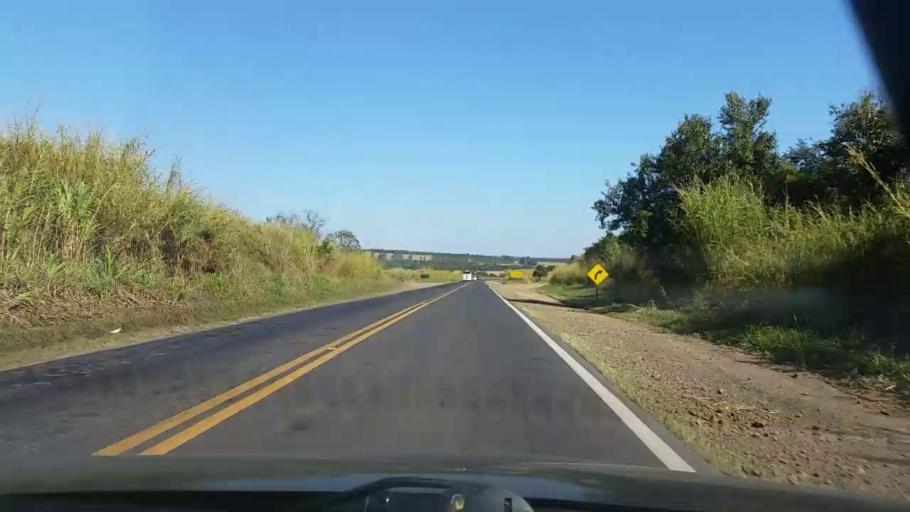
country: BR
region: Sao Paulo
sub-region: Itatinga
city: Itatinga
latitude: -22.9041
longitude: -48.7675
